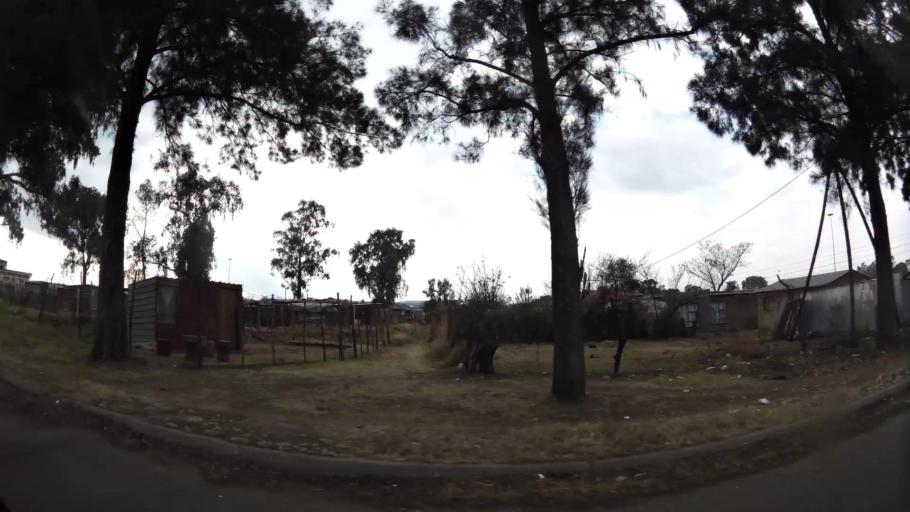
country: ZA
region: Gauteng
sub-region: Sedibeng District Municipality
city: Vanderbijlpark
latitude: -26.6713
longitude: 27.8412
